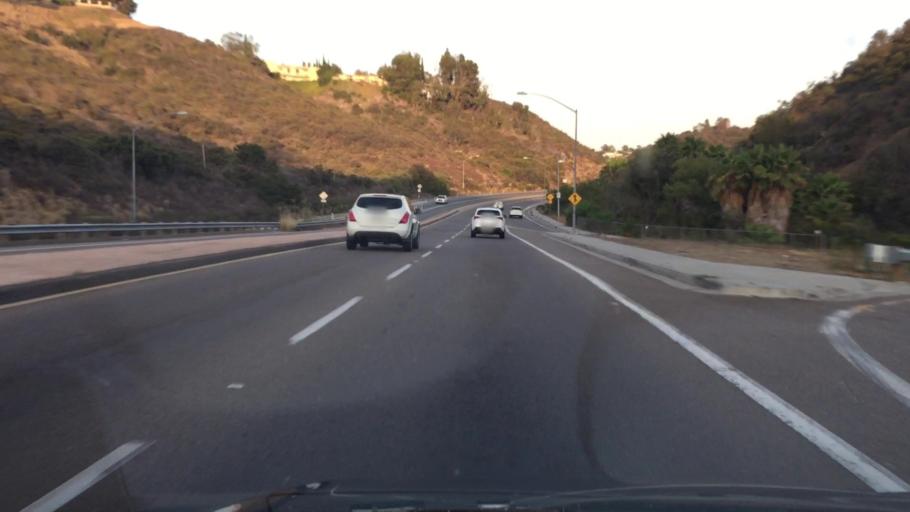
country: US
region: California
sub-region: San Diego County
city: Lemon Grove
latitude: 32.7722
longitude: -117.0964
